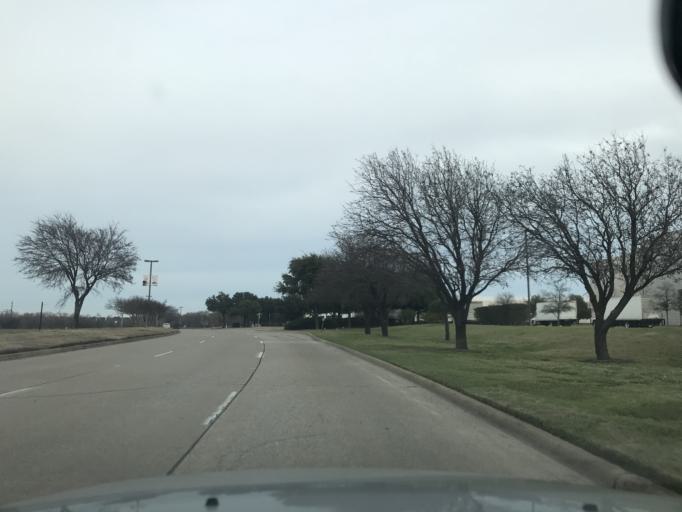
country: US
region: Texas
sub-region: Dallas County
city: Carrollton
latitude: 32.9947
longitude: -96.9309
